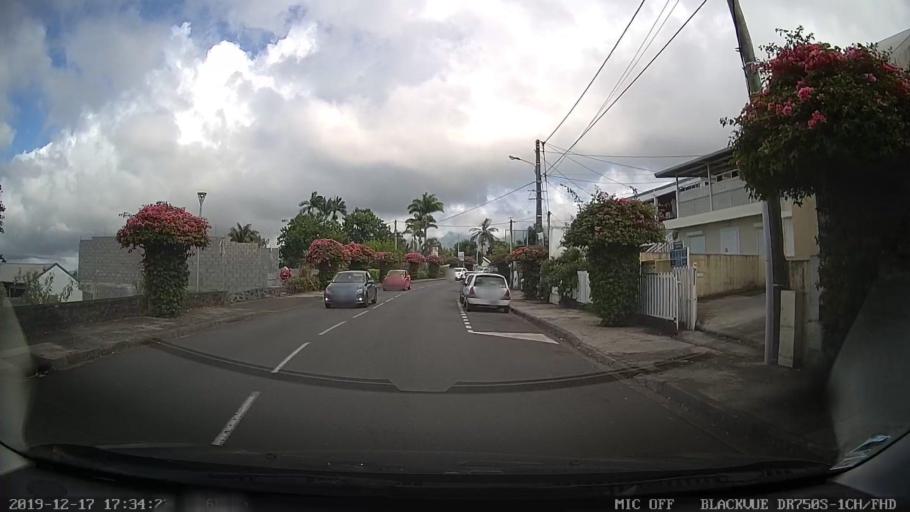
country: RE
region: Reunion
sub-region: Reunion
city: Le Tampon
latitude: -21.2707
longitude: 55.5107
